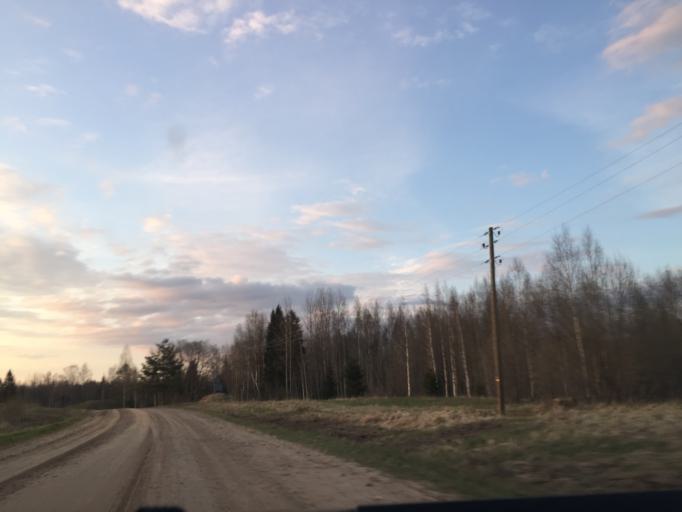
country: LV
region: Aluksnes Rajons
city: Aluksne
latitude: 57.2938
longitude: 26.9187
